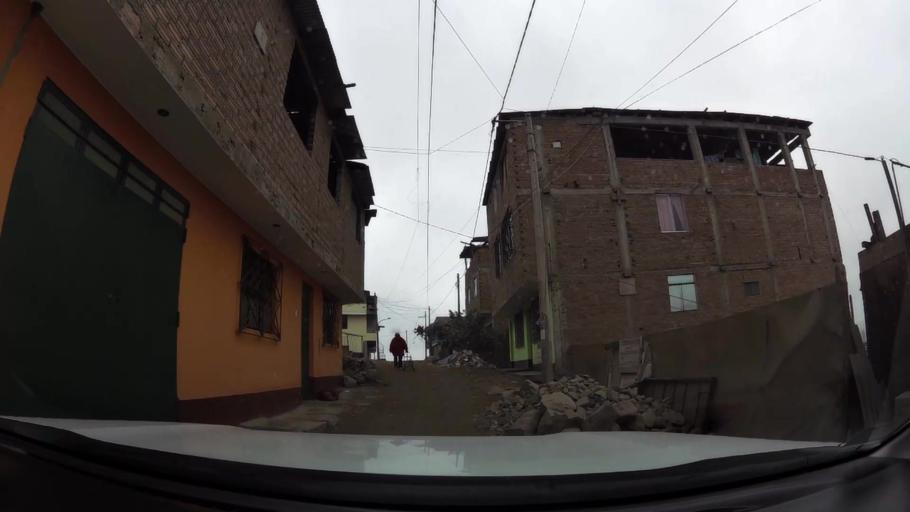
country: PE
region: Lima
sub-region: Lima
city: Surco
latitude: -12.1665
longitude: -76.9573
